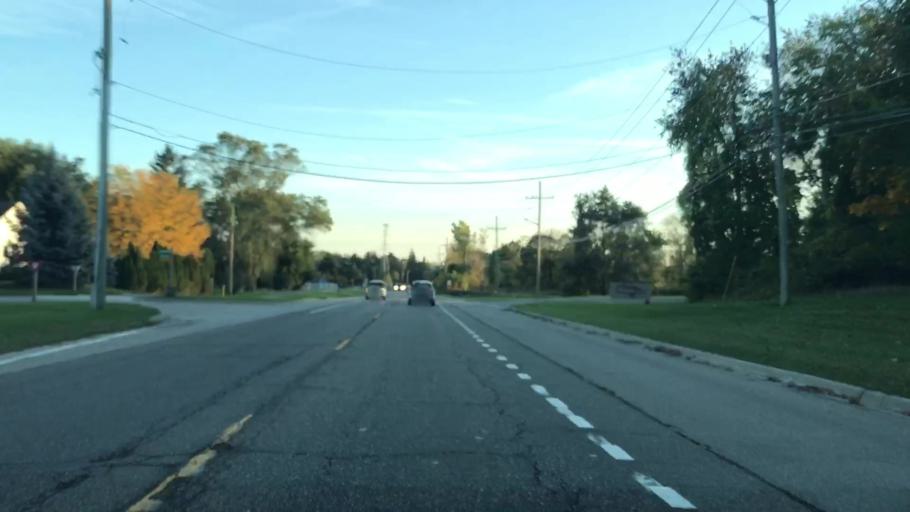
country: US
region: Michigan
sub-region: Oakland County
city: Rochester
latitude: 42.6788
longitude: -83.0940
